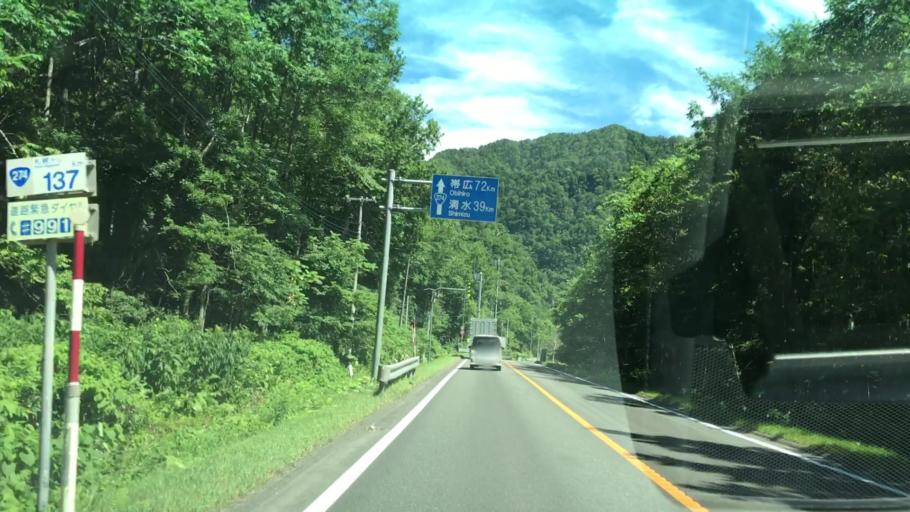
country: JP
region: Hokkaido
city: Shimo-furano
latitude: 42.9325
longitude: 142.5949
